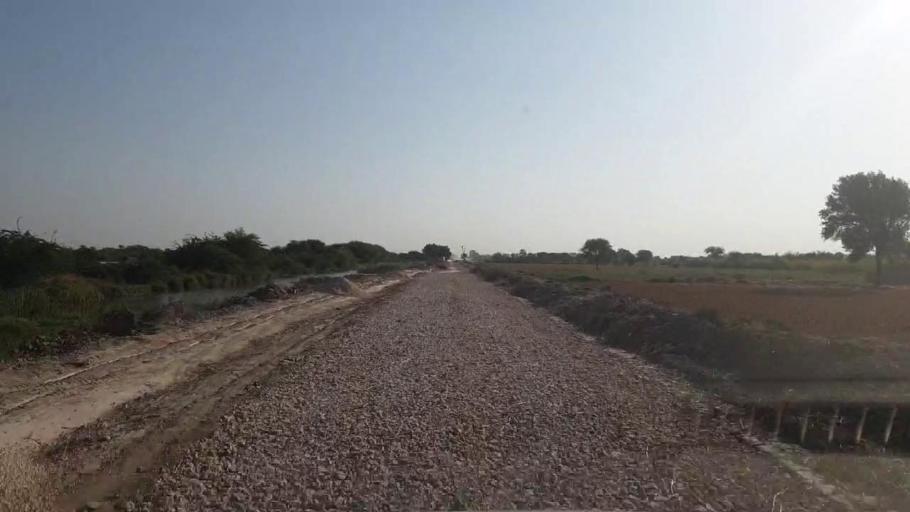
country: PK
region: Sindh
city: Talhar
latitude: 24.9275
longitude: 68.7482
